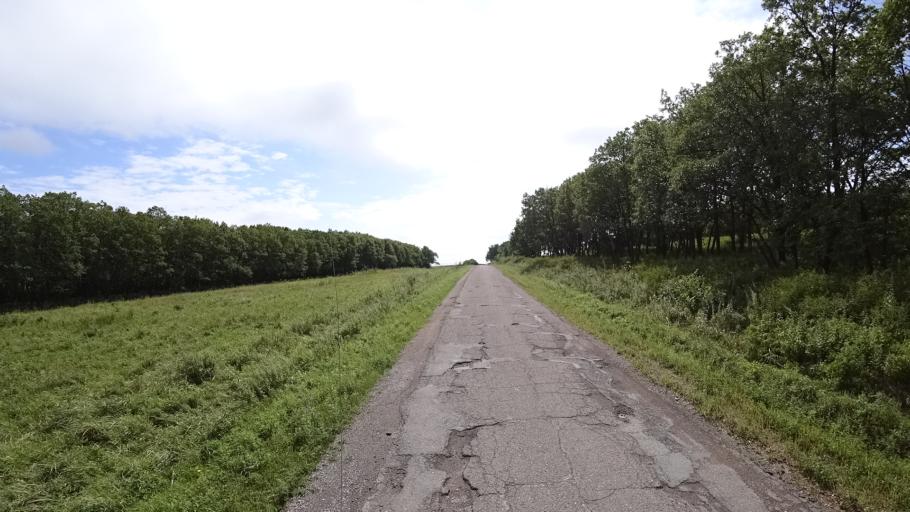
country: RU
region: Primorskiy
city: Lyalichi
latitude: 44.1458
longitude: 132.3901
